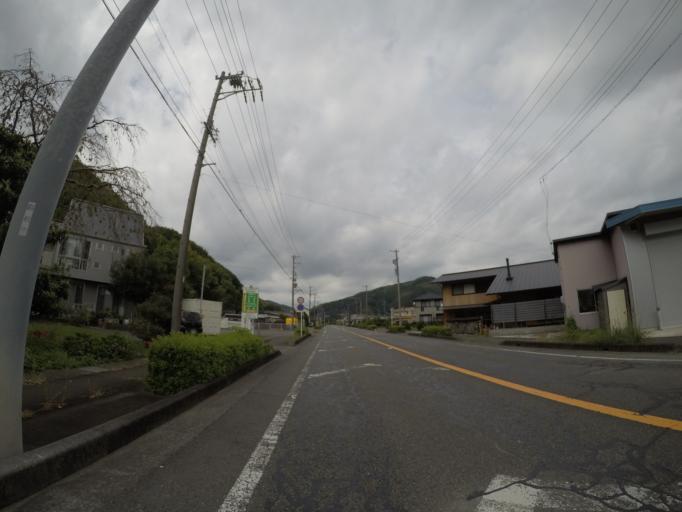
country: JP
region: Shizuoka
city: Fujieda
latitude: 34.8738
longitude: 138.2258
